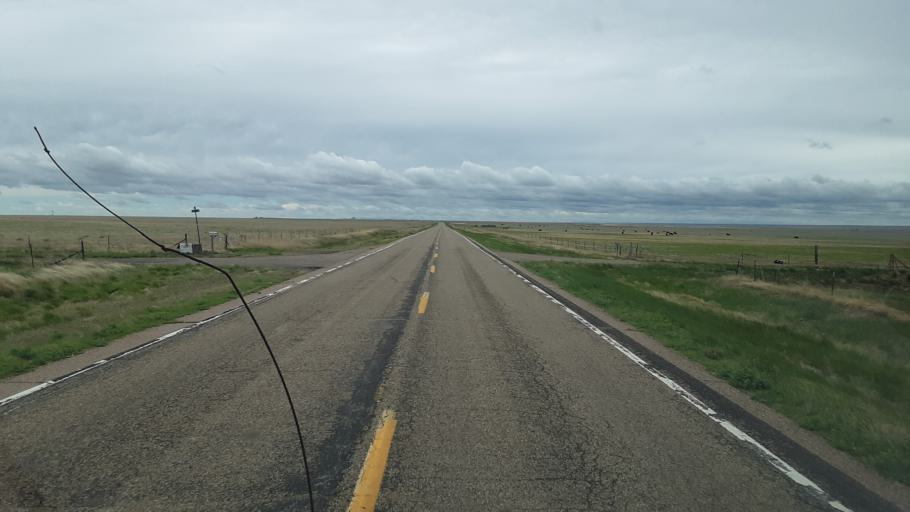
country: US
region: Colorado
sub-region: Lincoln County
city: Hugo
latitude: 38.8522
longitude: -103.7747
